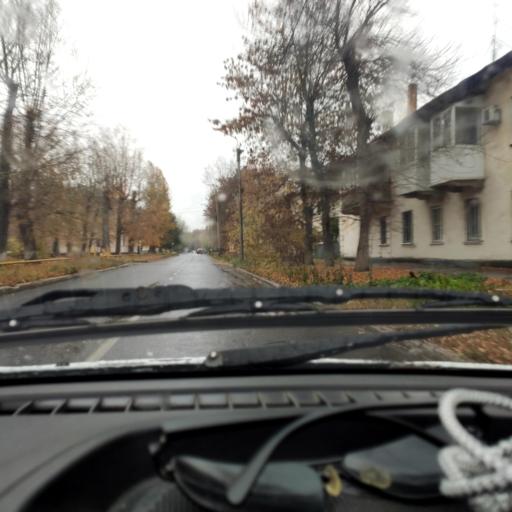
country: RU
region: Samara
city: Tol'yatti
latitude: 53.5041
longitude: 49.3916
